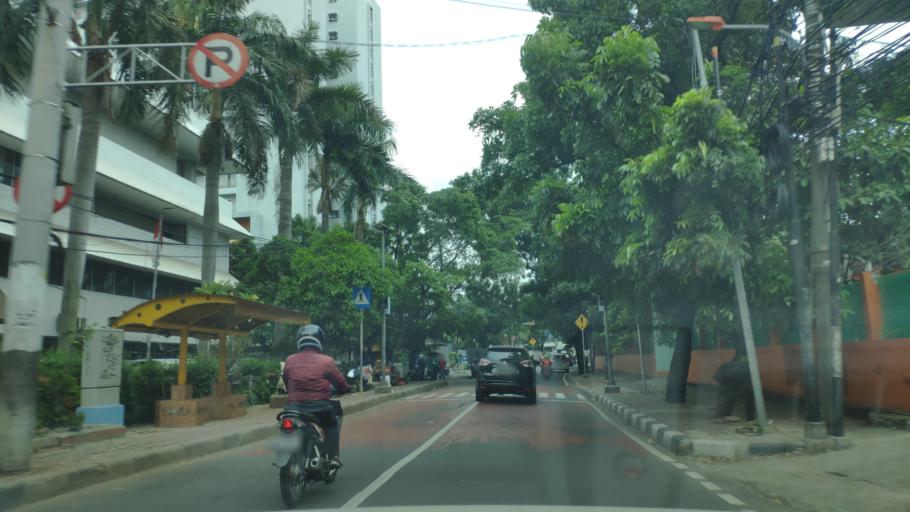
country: ID
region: Jakarta Raya
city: Jakarta
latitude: -6.1924
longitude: 106.7822
